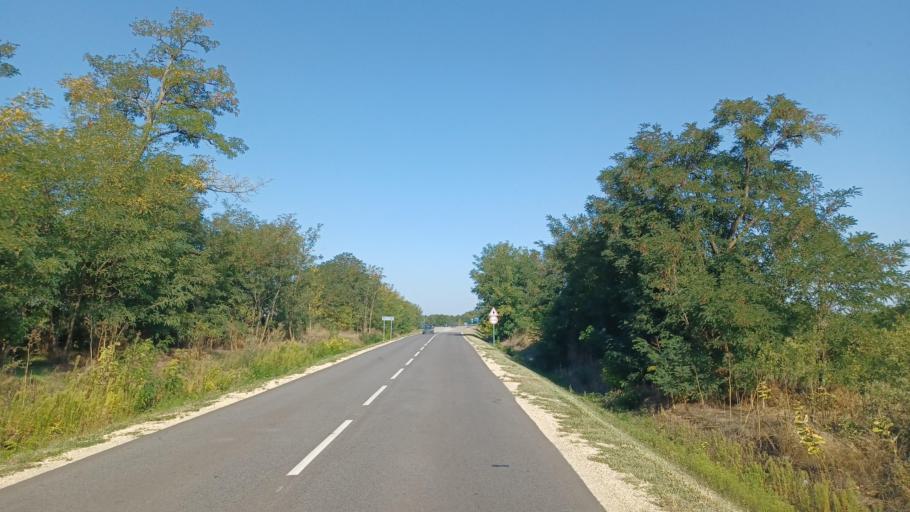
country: HU
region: Tolna
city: Paks
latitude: 46.6694
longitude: 18.8189
